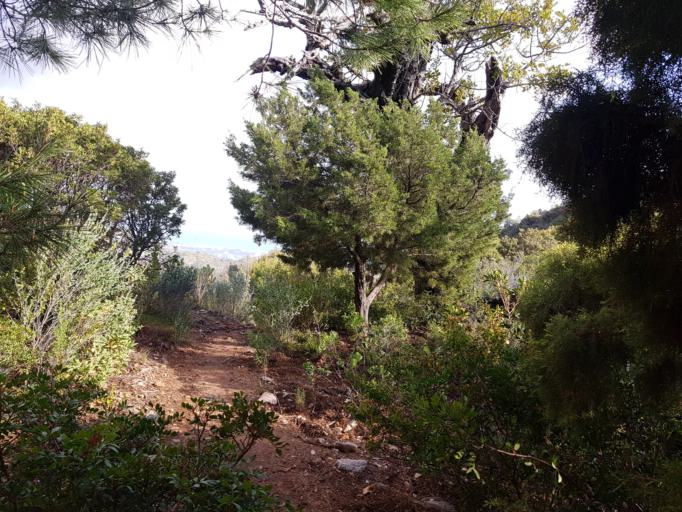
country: ES
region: Andalusia
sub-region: Provincia de Malaga
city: Marbella
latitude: 36.5501
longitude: -4.8926
